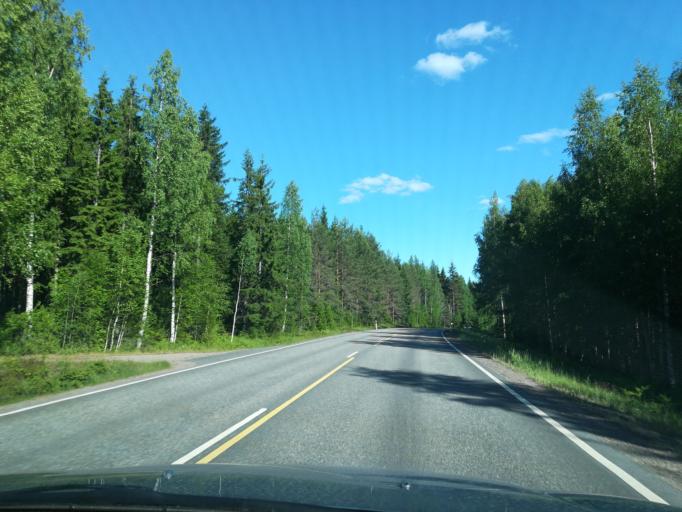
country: FI
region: South Karelia
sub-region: Imatra
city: Ruokolahti
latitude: 61.3896
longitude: 28.6465
